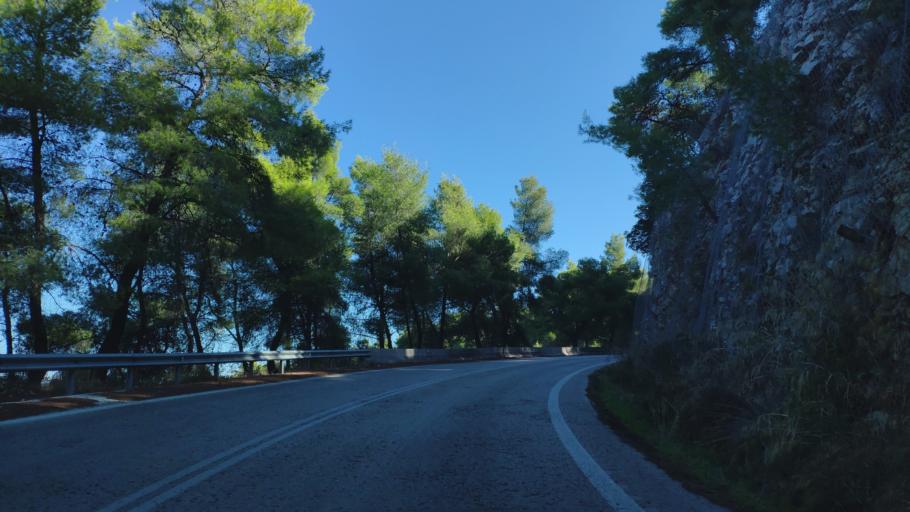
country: GR
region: Peloponnese
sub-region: Nomos Korinthias
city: Sofikon
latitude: 37.8279
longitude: 23.0741
